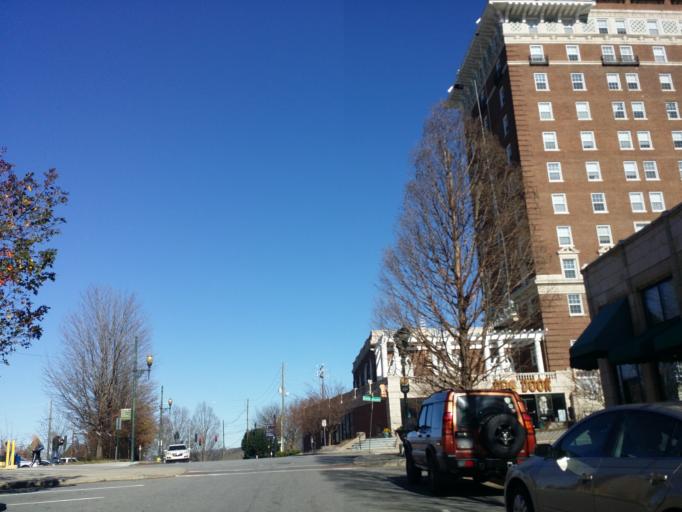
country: US
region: North Carolina
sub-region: Buncombe County
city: Asheville
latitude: 35.5958
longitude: -82.5571
